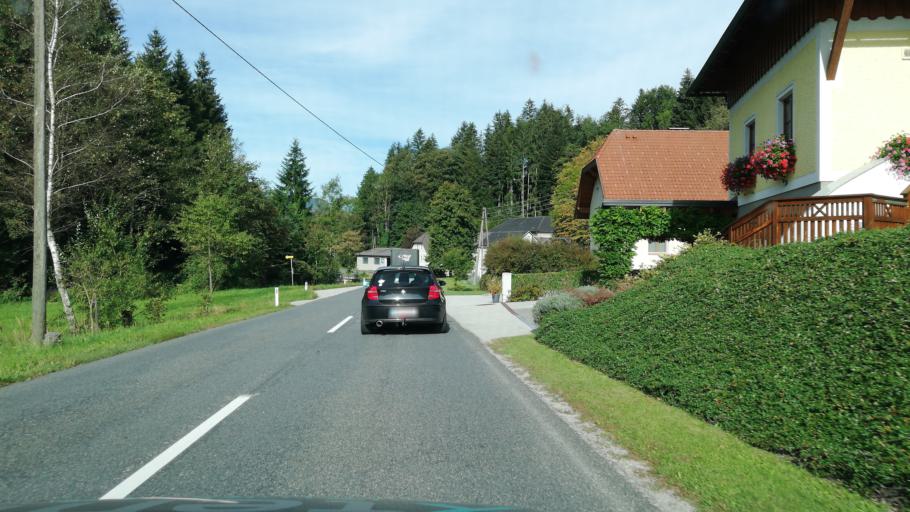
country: AT
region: Lower Austria
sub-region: Politischer Bezirk Amstetten
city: Behamberg
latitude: 47.9893
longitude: 14.5341
